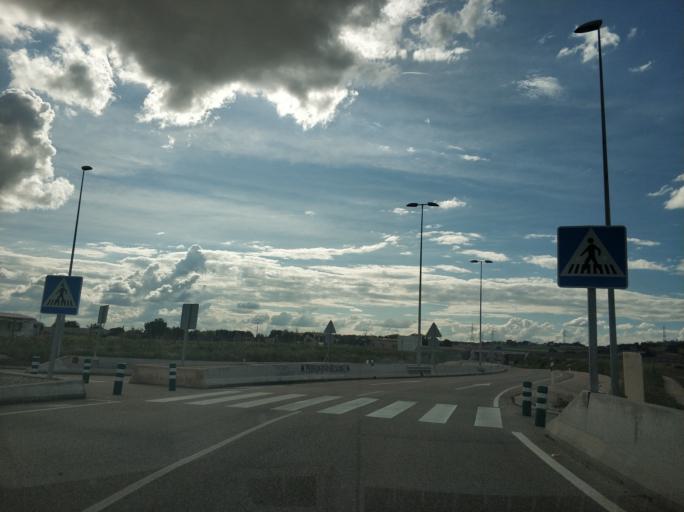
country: ES
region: Castille and Leon
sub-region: Provincia de Burgos
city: Aranda de Duero
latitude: 41.6921
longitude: -3.6694
